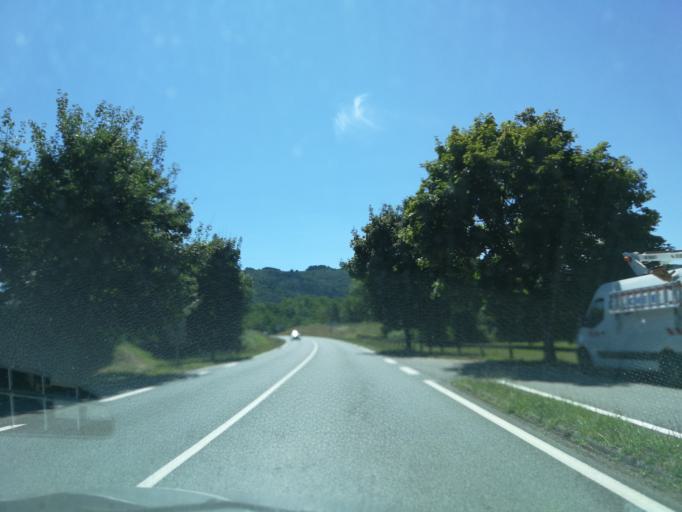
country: FR
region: Limousin
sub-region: Departement de la Correze
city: Argentat
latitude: 45.0885
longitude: 1.9343
